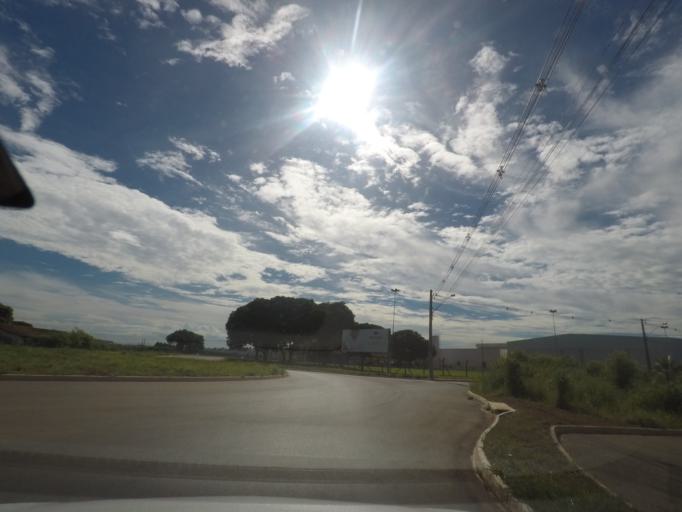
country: BR
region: Goias
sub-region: Aparecida De Goiania
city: Aparecida de Goiania
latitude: -16.8082
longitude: -49.2731
